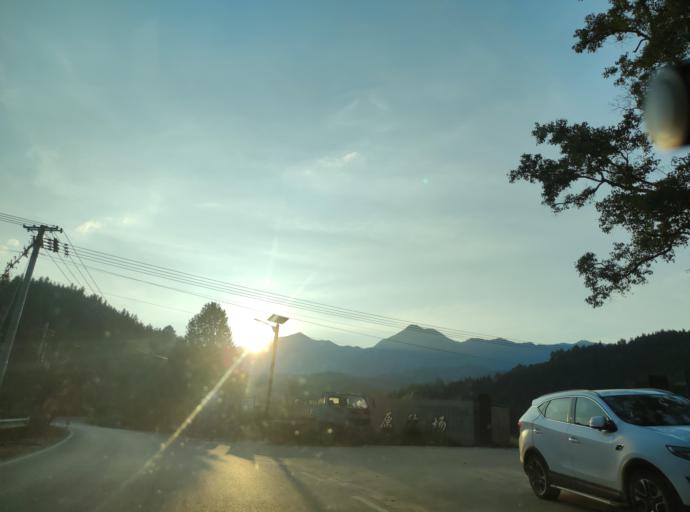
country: CN
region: Jiangxi Sheng
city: Zhangjiafang
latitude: 27.5283
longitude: 114.0283
